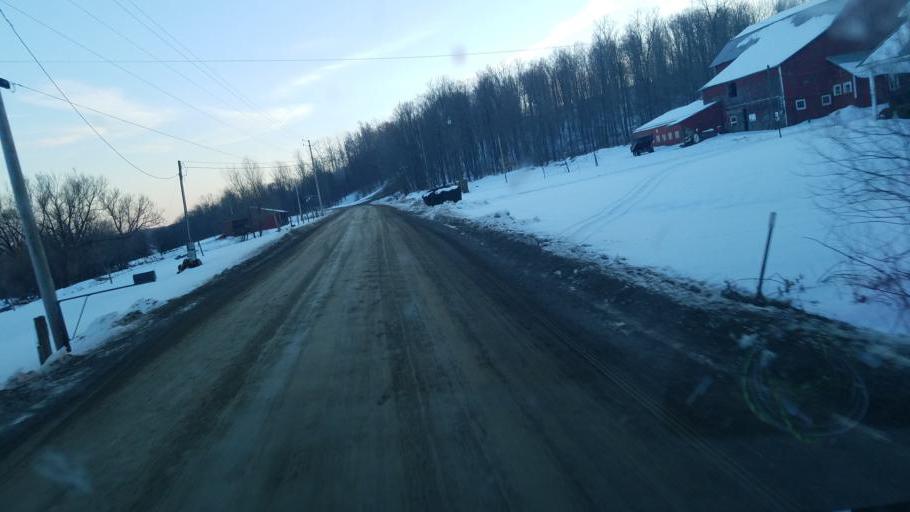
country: US
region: Pennsylvania
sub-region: Tioga County
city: Westfield
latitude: 42.0163
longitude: -77.6568
